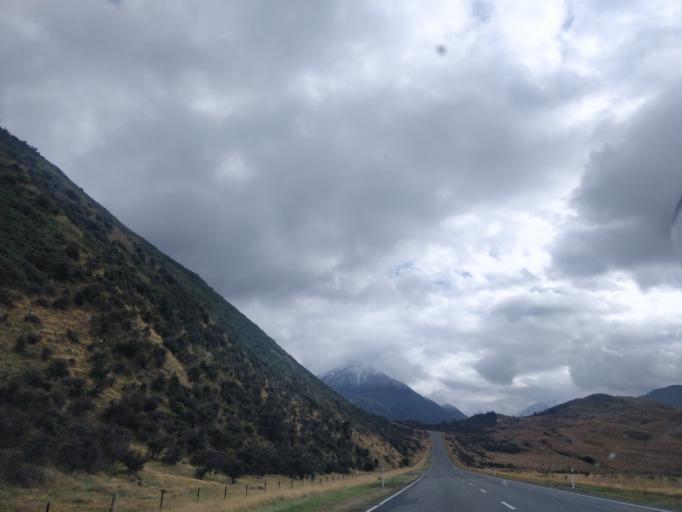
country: NZ
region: Canterbury
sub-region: Waimakariri District
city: Oxford
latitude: -43.0226
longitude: 171.7476
